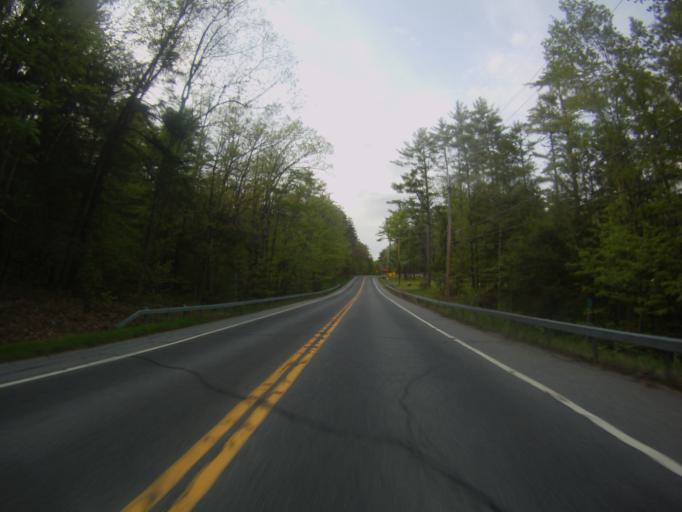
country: US
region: New York
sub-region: Essex County
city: Ticonderoga
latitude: 43.7914
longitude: -73.4875
